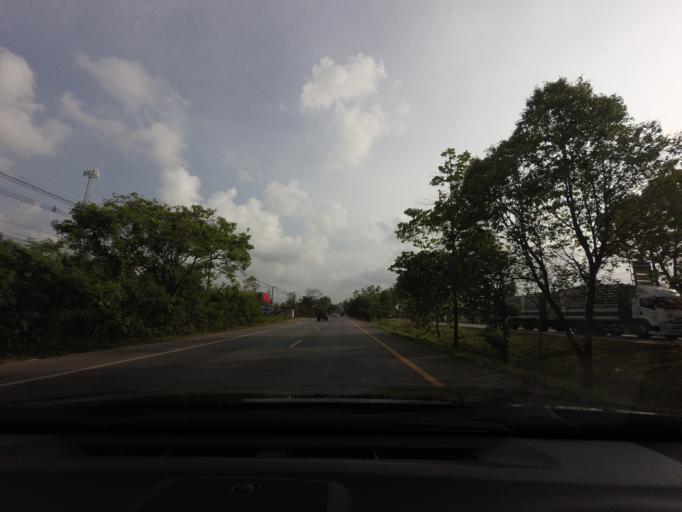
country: TH
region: Chumphon
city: Thung Tako
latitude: 10.1226
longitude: 99.0873
